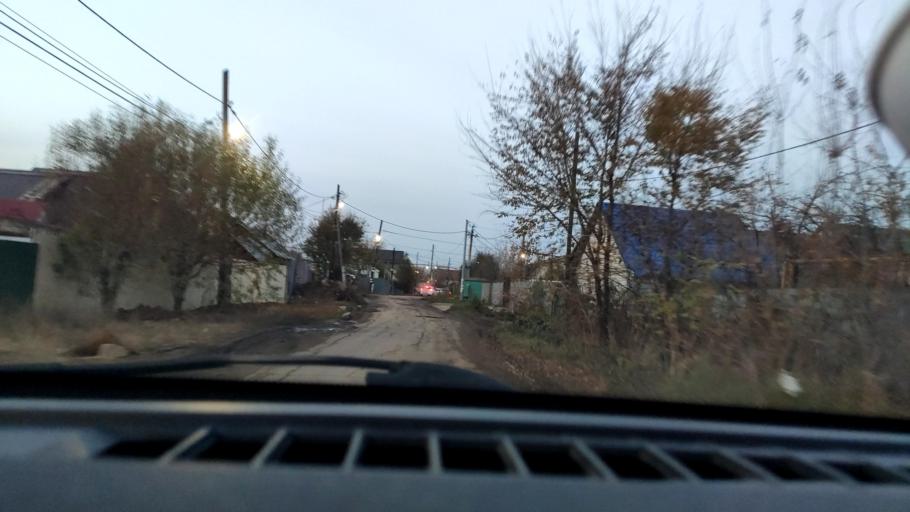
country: RU
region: Samara
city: Samara
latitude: 53.1383
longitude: 50.0960
